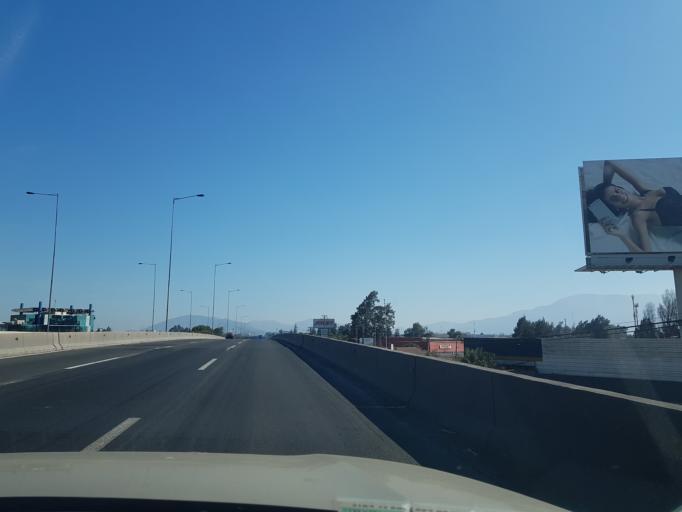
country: CL
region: Santiago Metropolitan
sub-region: Provincia de Santiago
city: Lo Prado
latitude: -33.3753
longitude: -70.7473
